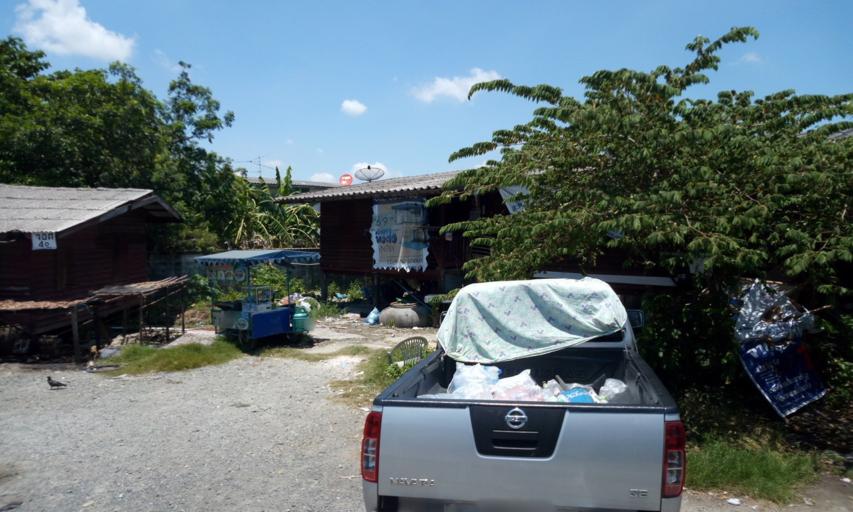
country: TH
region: Bangkok
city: Bang Na
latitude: 13.6059
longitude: 100.7103
